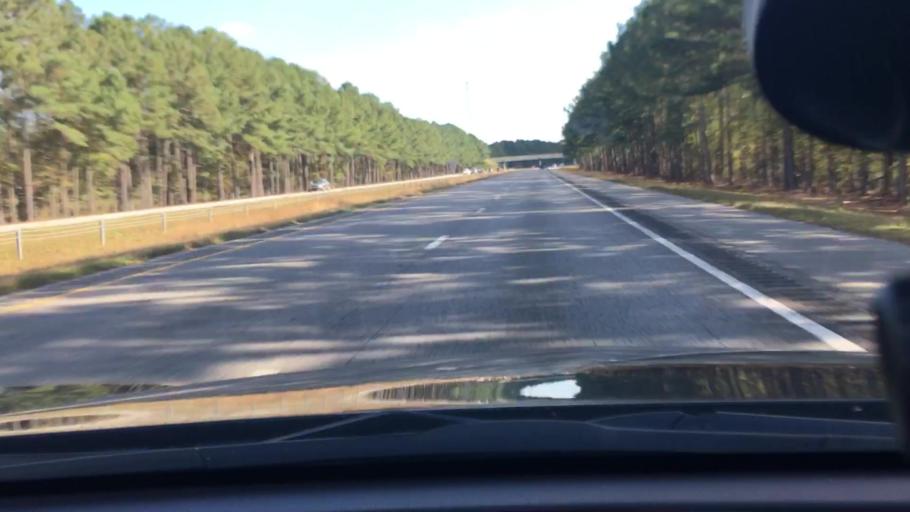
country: US
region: North Carolina
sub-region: Edgecombe County
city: Pinetops
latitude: 35.6577
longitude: -77.7485
